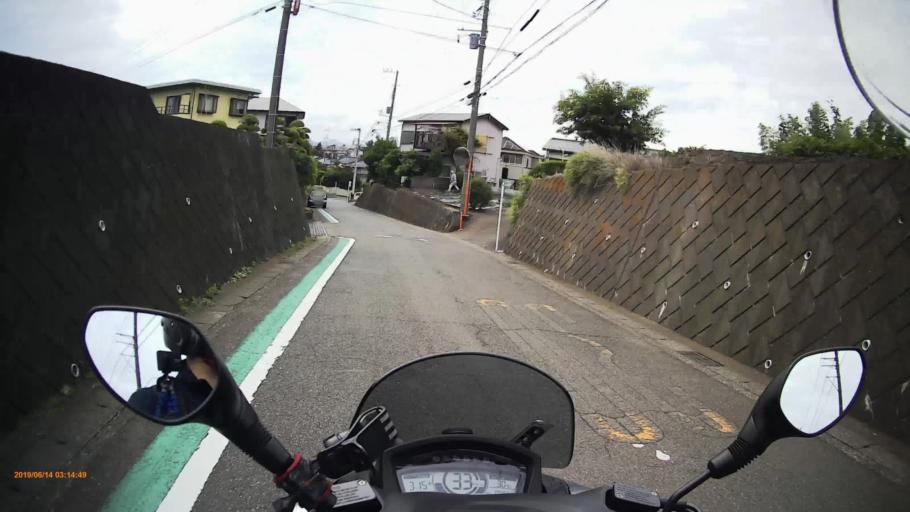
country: JP
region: Kanagawa
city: Fujisawa
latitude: 35.4124
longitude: 139.4596
